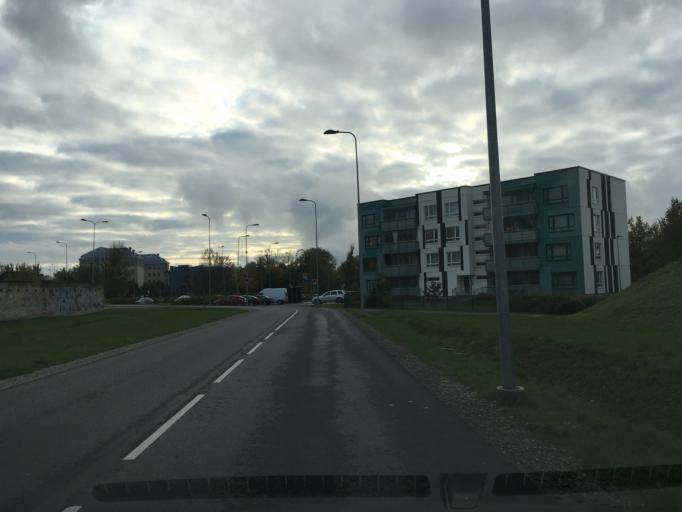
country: EE
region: Harju
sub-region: Tallinna linn
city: Tallinn
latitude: 59.4308
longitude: 24.8050
